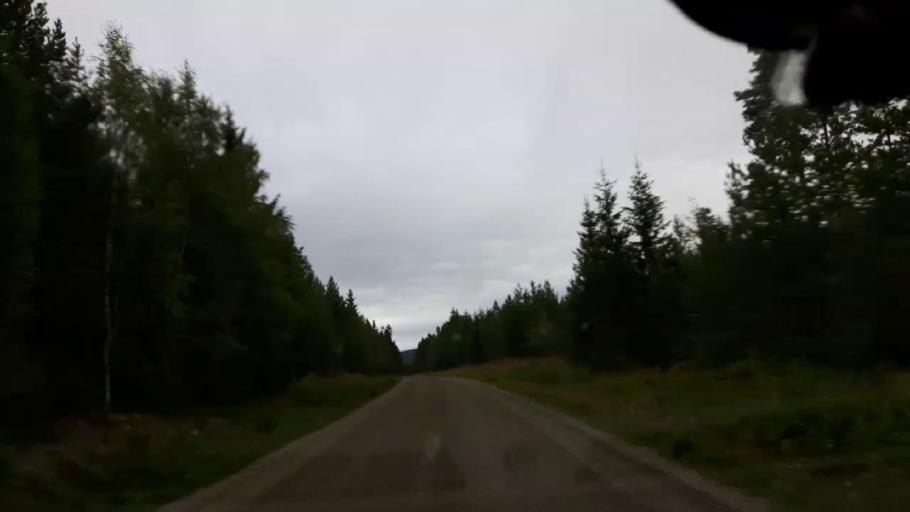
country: SE
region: Jaemtland
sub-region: Braecke Kommun
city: Braecke
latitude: 62.9387
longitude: 15.4573
